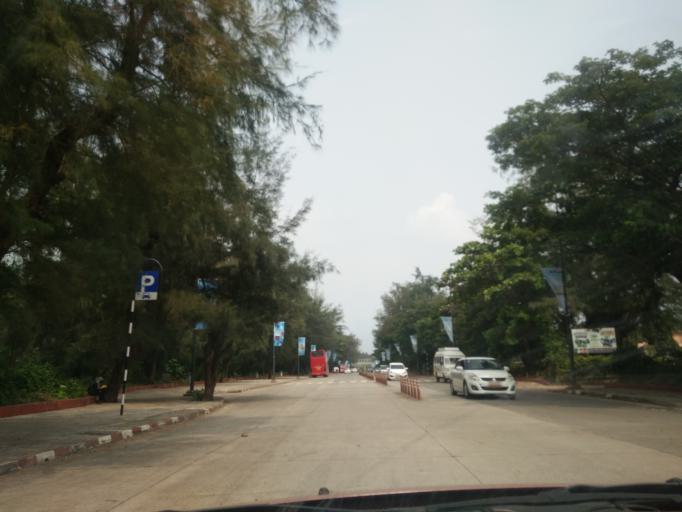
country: IN
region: Goa
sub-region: North Goa
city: Taleigao
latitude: 15.4771
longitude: 73.8083
